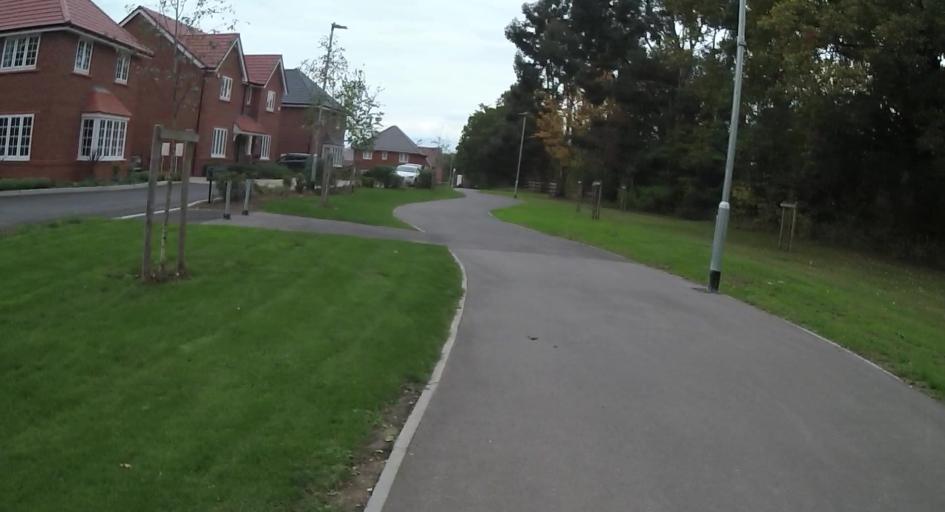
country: GB
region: England
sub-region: Bracknell Forest
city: Binfield
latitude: 51.4251
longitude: -0.7762
